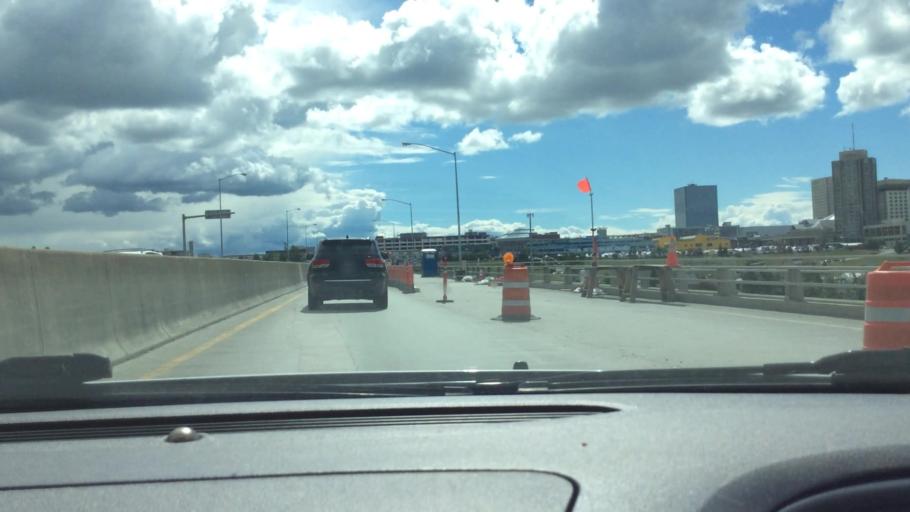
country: US
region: Alaska
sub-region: Anchorage Municipality
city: Anchorage
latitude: 61.2250
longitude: -149.8852
